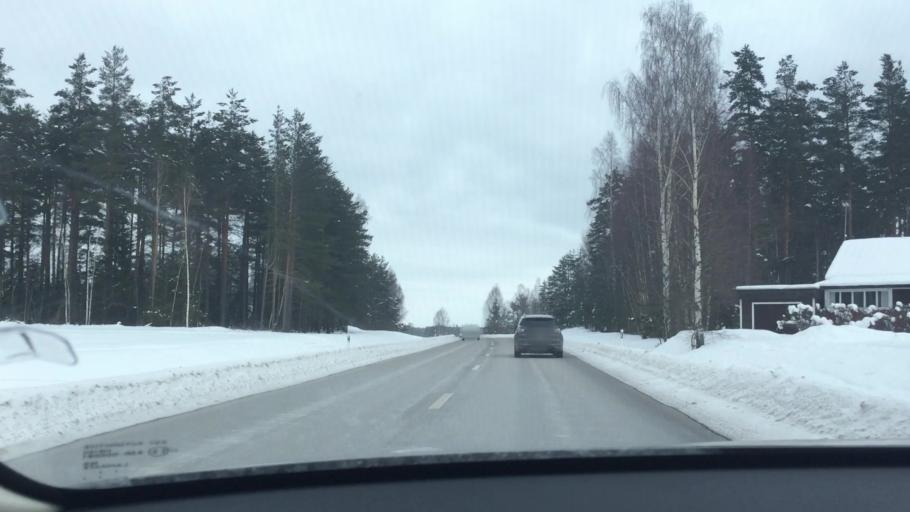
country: SE
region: Dalarna
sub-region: Faluns Kommun
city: Svardsjo
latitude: 60.6377
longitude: 15.8386
